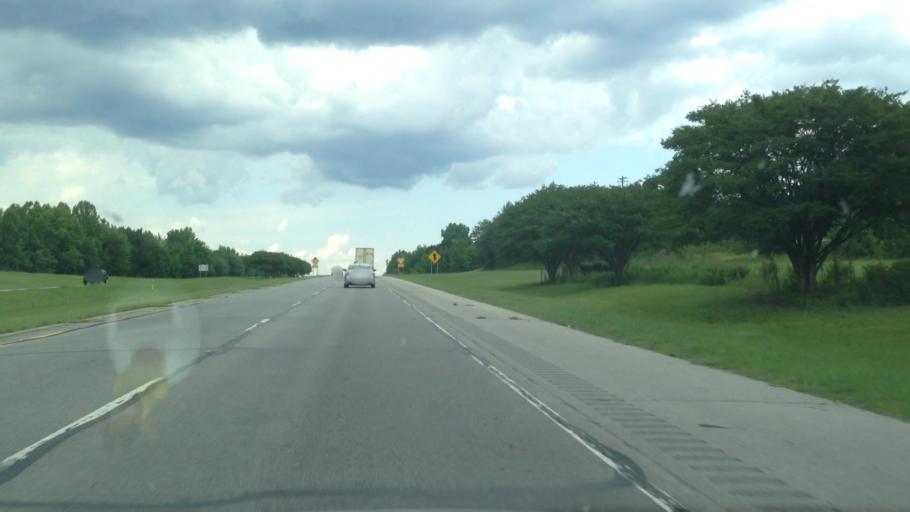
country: US
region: Virginia
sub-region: City of Danville
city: Danville
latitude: 36.5202
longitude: -79.4739
